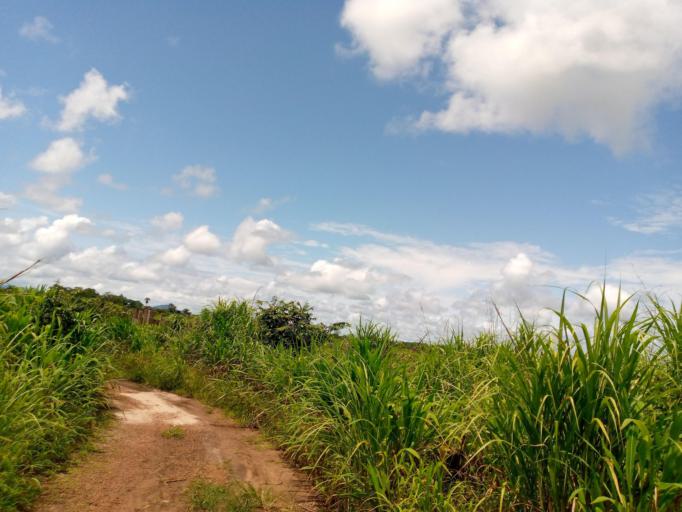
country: SL
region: Northern Province
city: Magburaka
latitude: 8.7171
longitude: -11.9220
